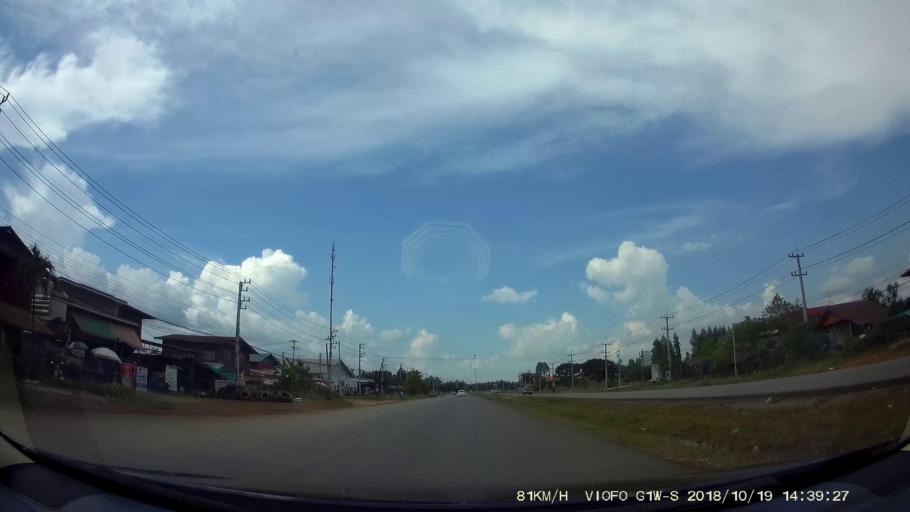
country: TH
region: Chaiyaphum
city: Kaeng Khro
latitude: 16.2261
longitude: 102.1950
